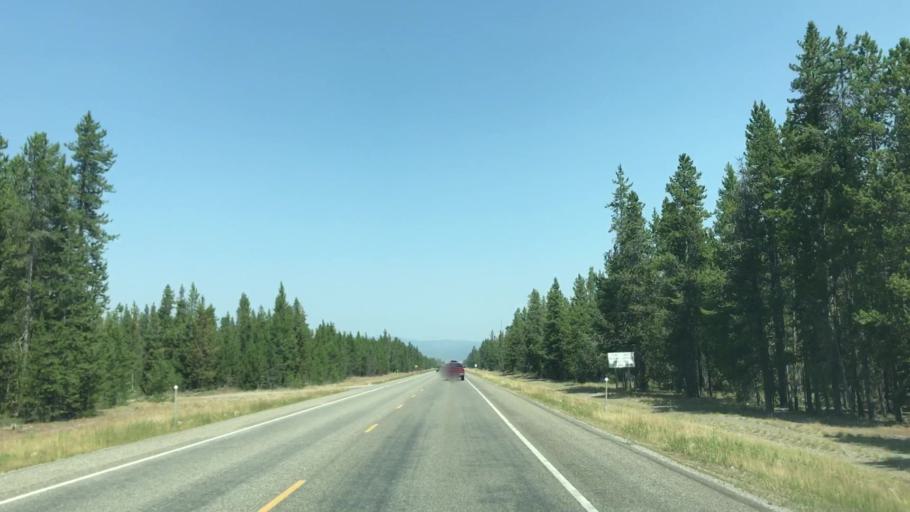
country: US
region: Montana
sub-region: Gallatin County
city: West Yellowstone
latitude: 44.6791
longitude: -111.1007
